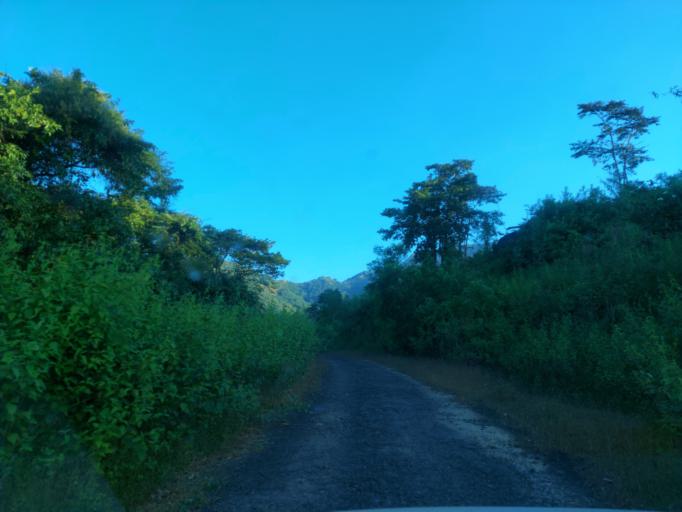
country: IN
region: Maharashtra
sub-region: Sindhudurg
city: Kudal
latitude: 16.0768
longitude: 73.8265
